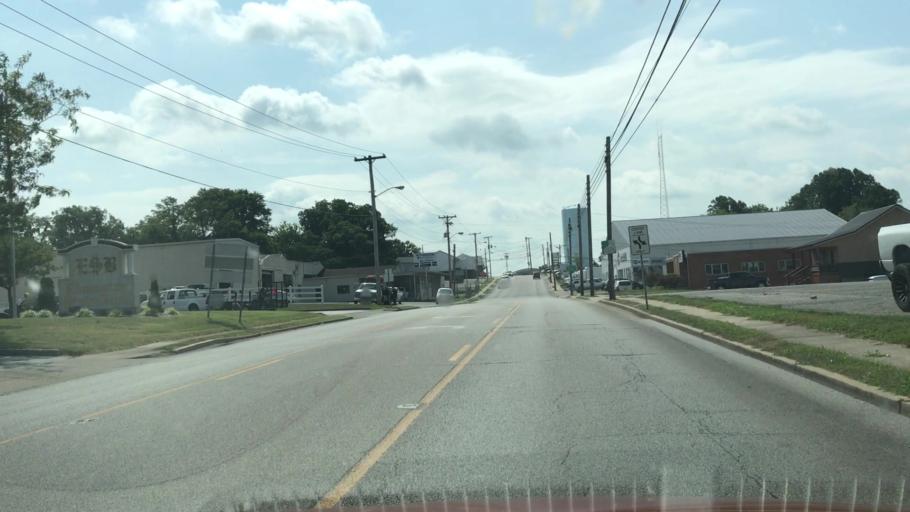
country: US
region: Kentucky
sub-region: Barren County
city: Glasgow
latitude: 37.0014
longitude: -85.9253
